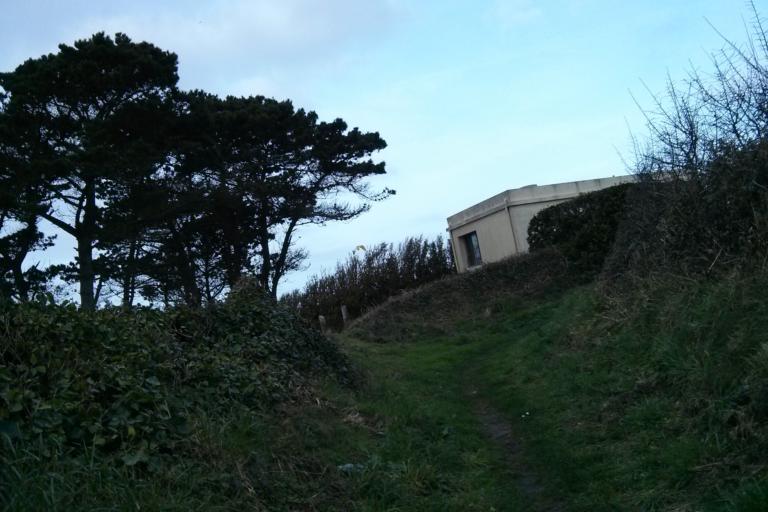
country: FR
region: Brittany
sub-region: Departement du Finistere
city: Le Conquet
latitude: 48.4031
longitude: -4.7733
